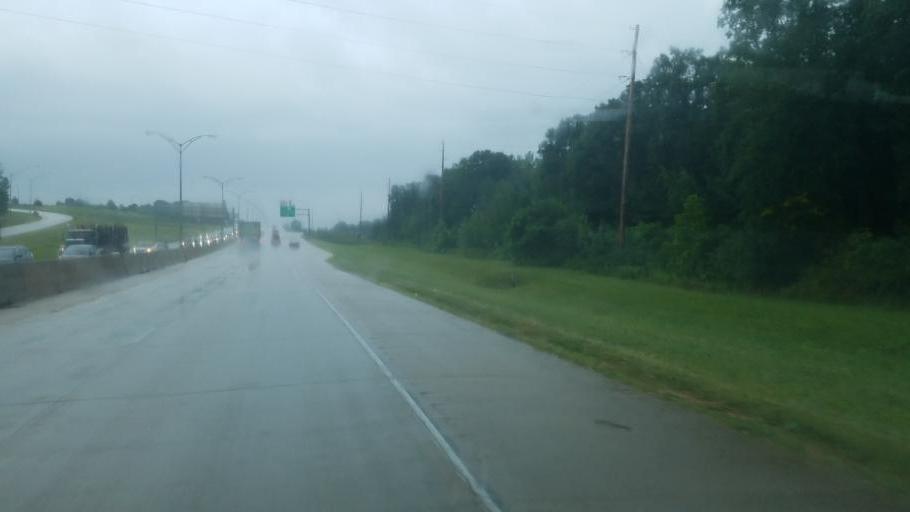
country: US
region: Ohio
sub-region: Trumbull County
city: Girard
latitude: 41.1382
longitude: -80.6798
